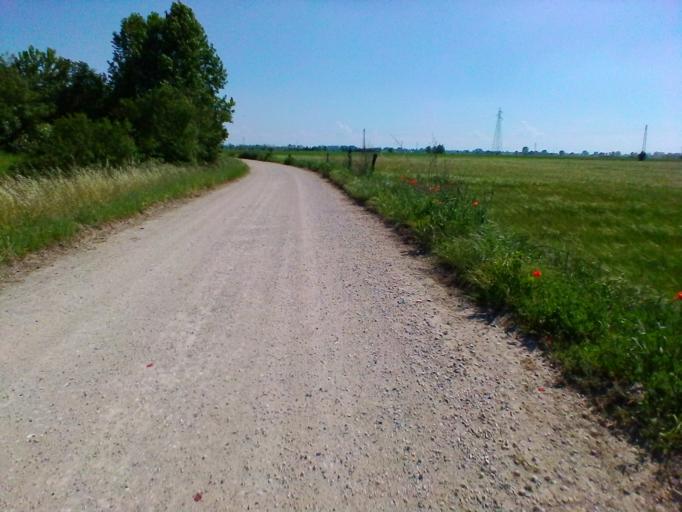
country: IT
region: Veneto
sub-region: Provincia di Verona
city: Povegliano Veronese
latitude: 45.3228
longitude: 10.8774
